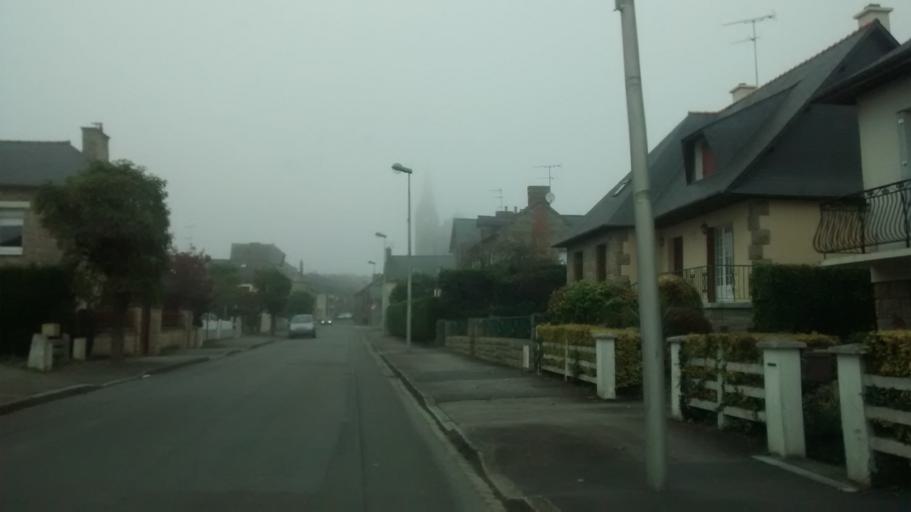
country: FR
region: Brittany
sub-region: Departement d'Ille-et-Vilaine
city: Liffre
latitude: 48.2119
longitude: -1.5045
